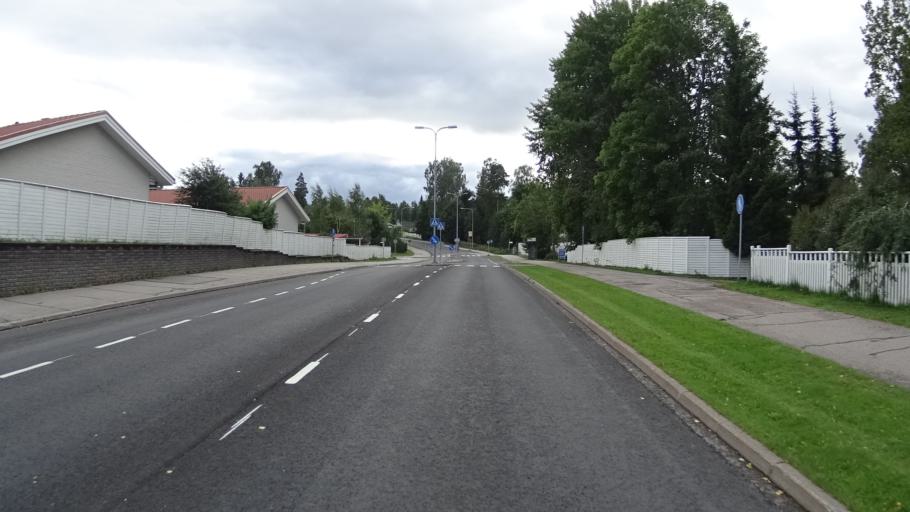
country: FI
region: Uusimaa
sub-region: Helsinki
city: Kauniainen
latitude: 60.2223
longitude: 24.7433
